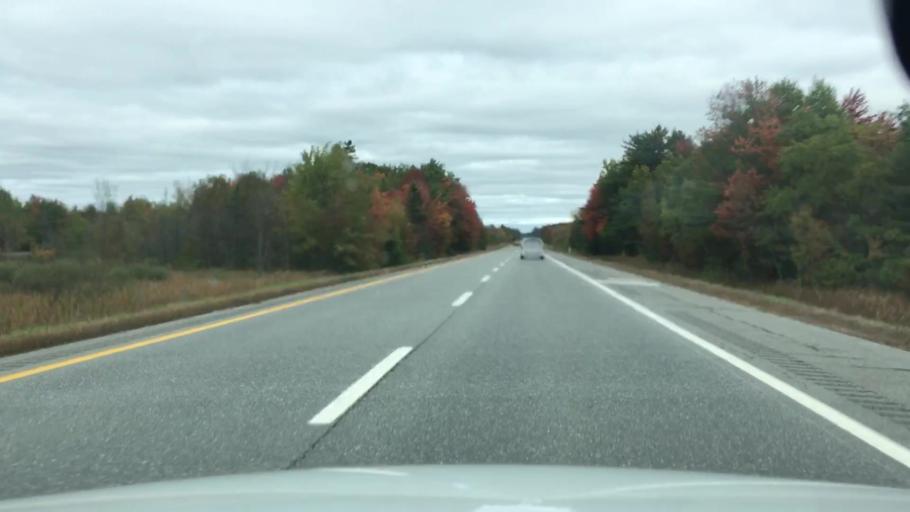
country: US
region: Maine
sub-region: Kennebec County
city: Benton
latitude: 44.6084
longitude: -69.5712
